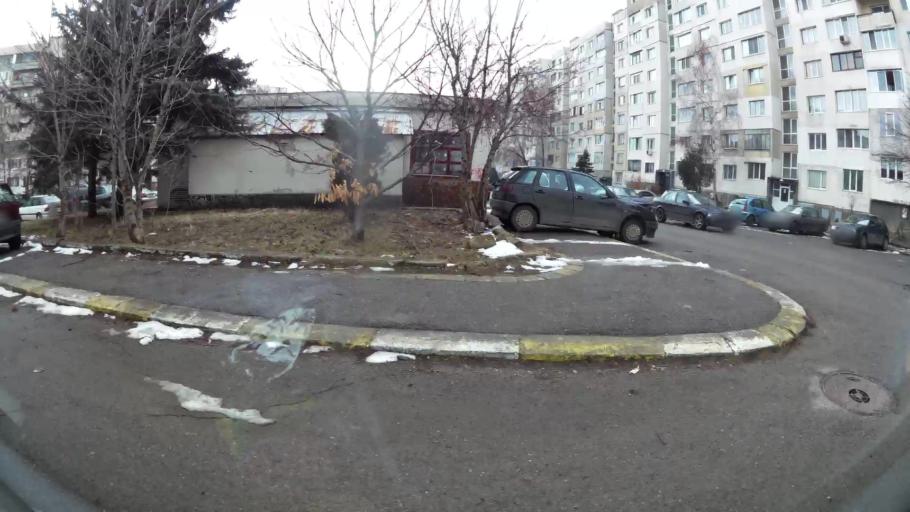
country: BG
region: Sofiya
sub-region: Obshtina Bozhurishte
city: Bozhurishte
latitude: 42.7142
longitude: 23.2381
